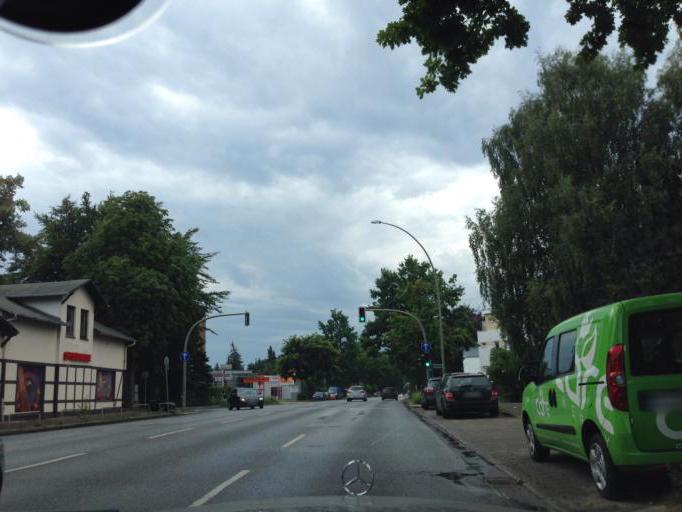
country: DE
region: Hamburg
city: Sasel
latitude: 53.6516
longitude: 10.1056
